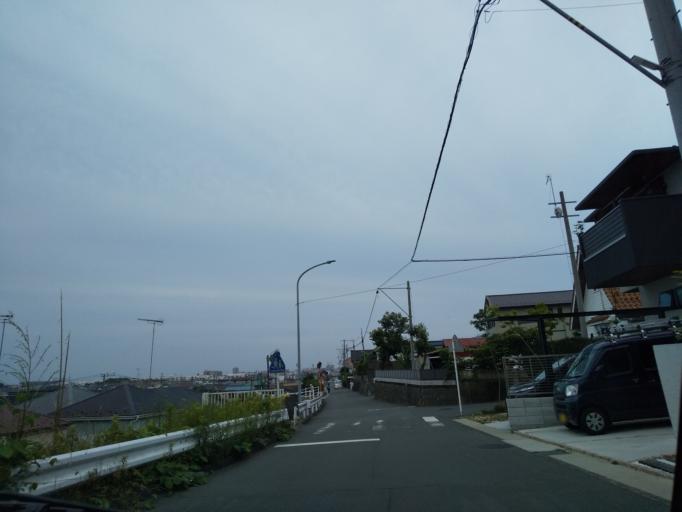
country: JP
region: Kanagawa
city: Atsugi
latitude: 35.4705
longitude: 139.3538
